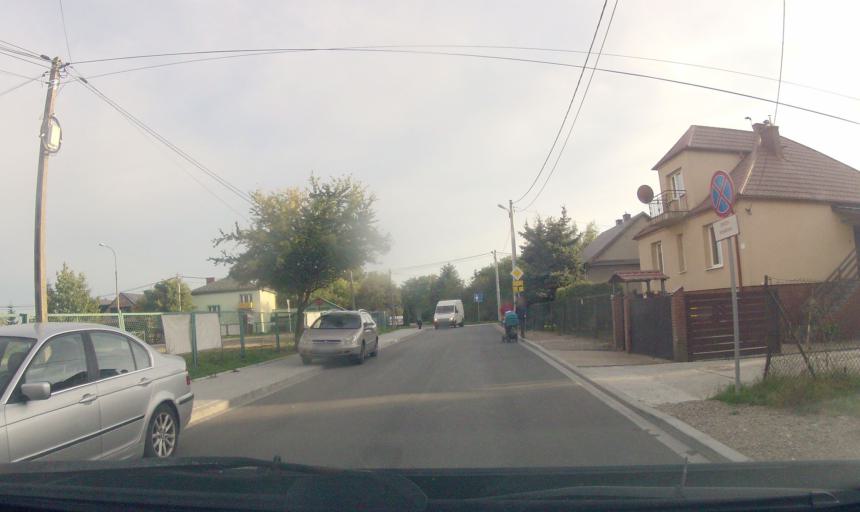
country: PL
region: Lesser Poland Voivodeship
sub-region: Krakow
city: Krakow
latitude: 50.0345
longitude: 19.9967
